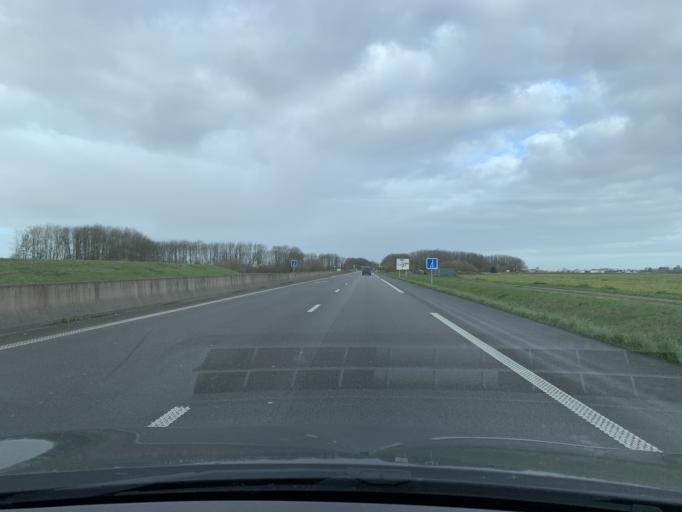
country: FR
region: Nord-Pas-de-Calais
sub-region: Departement du Nord
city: Goeulzin
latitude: 50.3244
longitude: 3.1141
